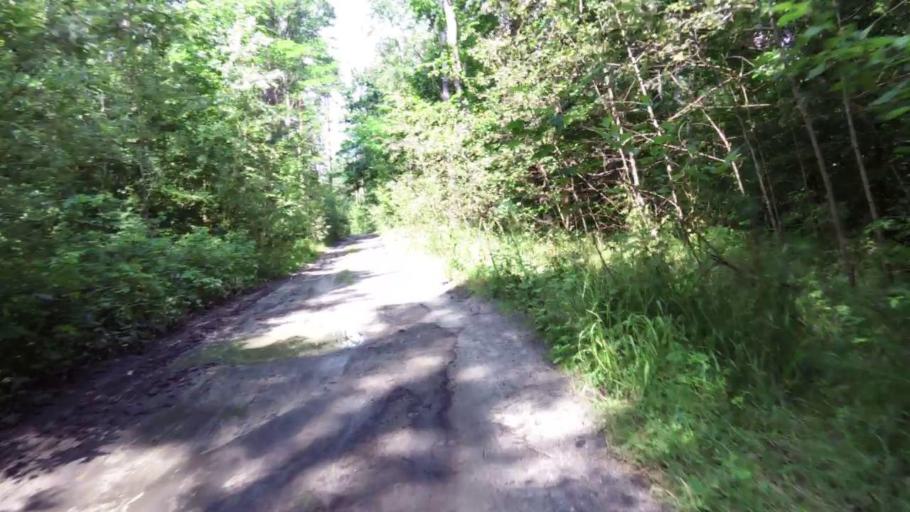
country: PL
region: West Pomeranian Voivodeship
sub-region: Powiat gryfinski
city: Stare Czarnowo
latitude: 53.3494
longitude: 14.7609
